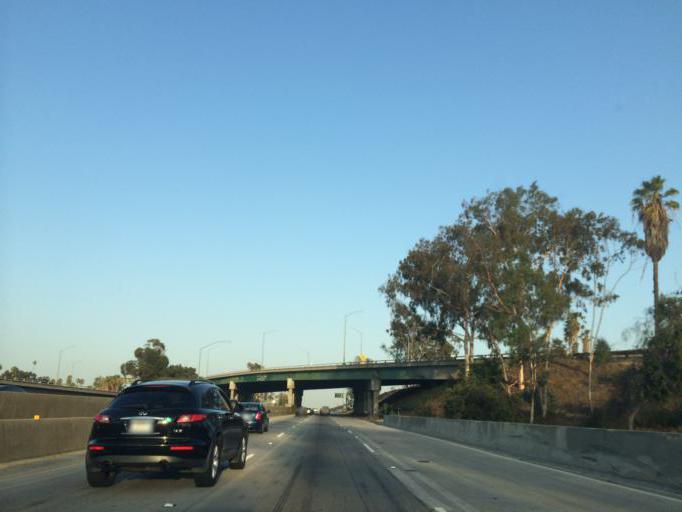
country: US
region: California
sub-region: Los Angeles County
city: Boyle Heights
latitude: 34.0300
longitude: -118.2165
